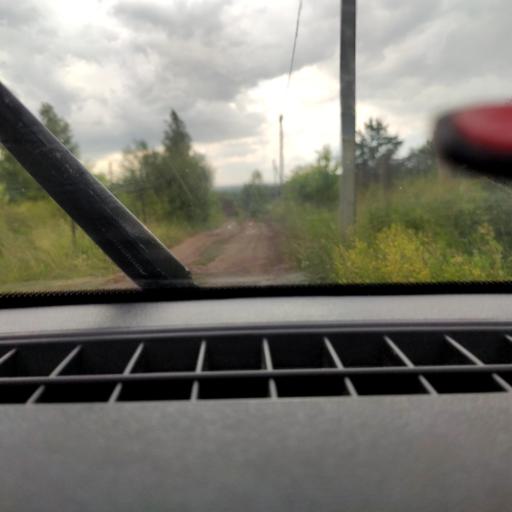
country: RU
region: Bashkortostan
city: Kabakovo
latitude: 54.5655
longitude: 56.2763
